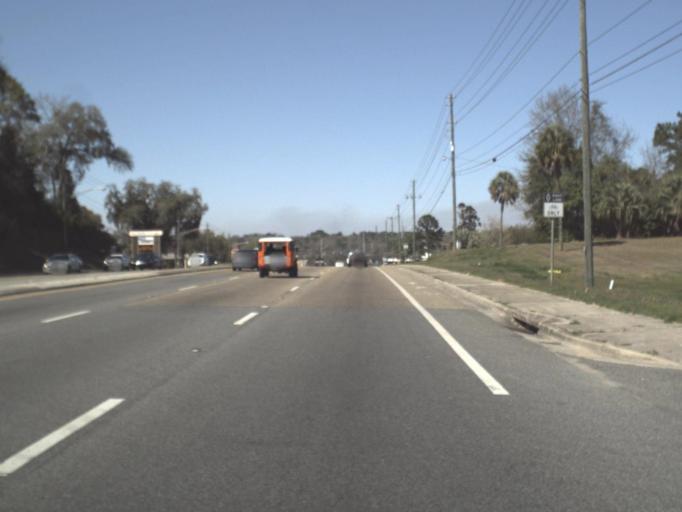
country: US
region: Florida
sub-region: Leon County
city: Tallahassee
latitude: 30.4483
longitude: -84.2264
